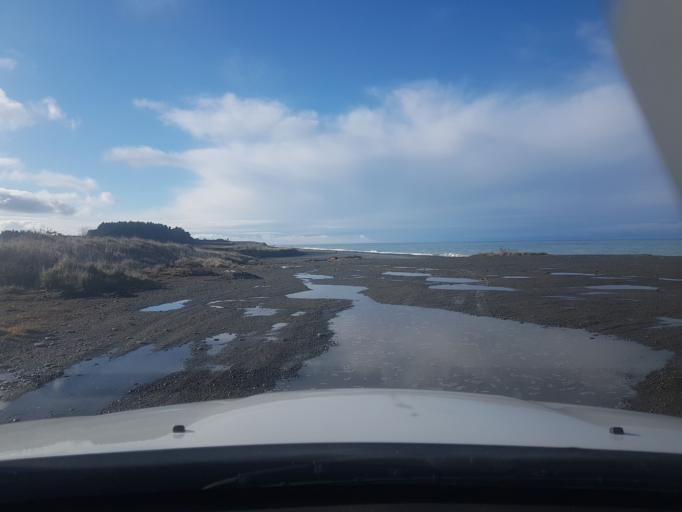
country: NZ
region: Canterbury
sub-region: Timaru District
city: Timaru
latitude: -44.4633
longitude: 171.2435
